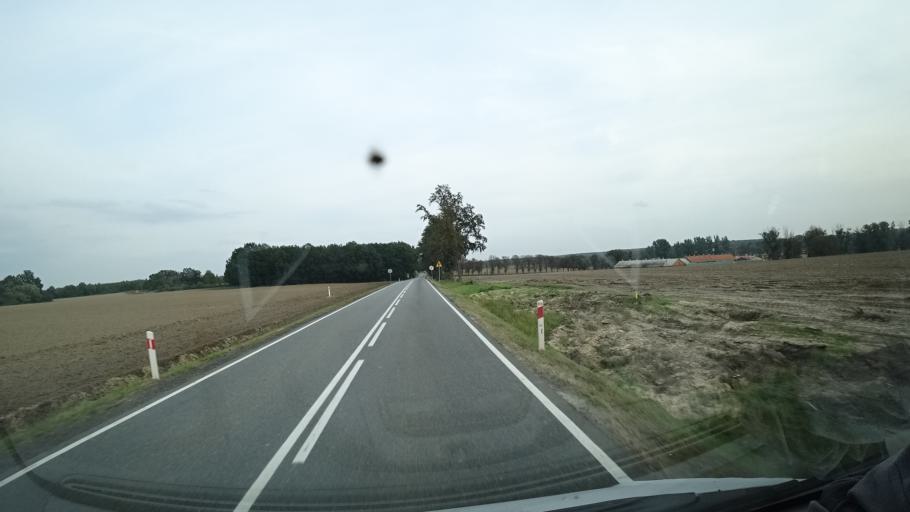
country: PL
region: Silesian Voivodeship
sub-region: Powiat gliwicki
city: Rudziniec
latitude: 50.3881
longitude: 18.3979
